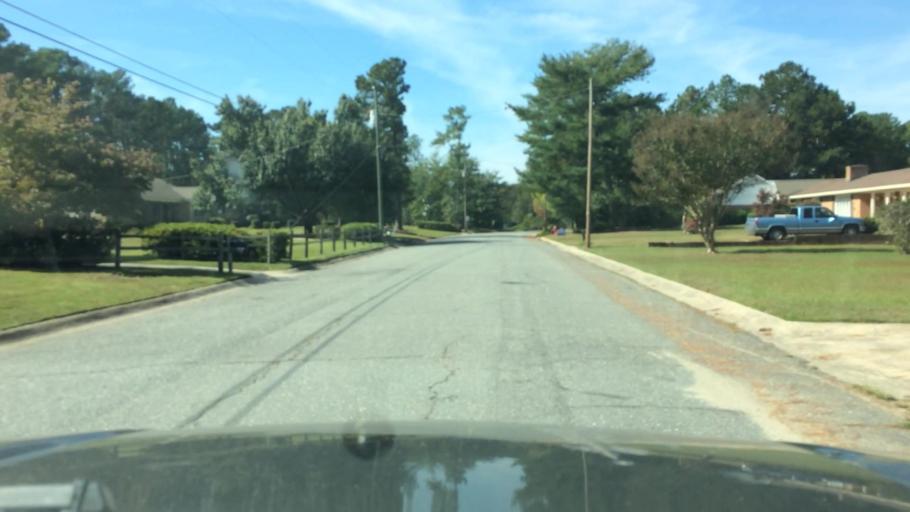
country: US
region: North Carolina
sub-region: Wayne County
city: Goldsboro
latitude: 35.3936
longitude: -77.9573
